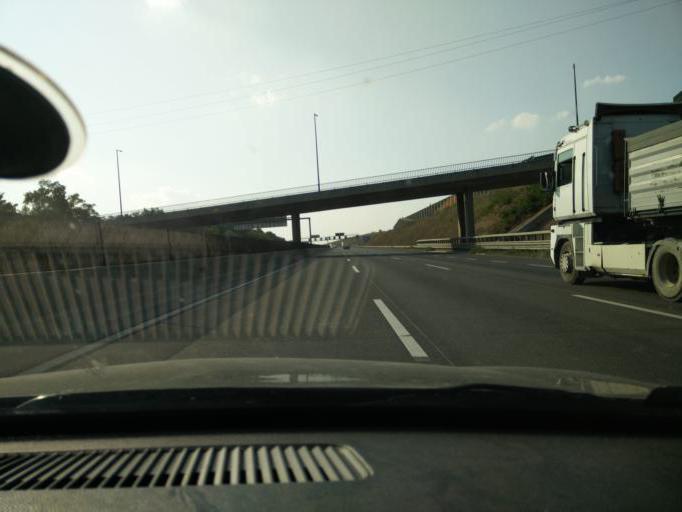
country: HU
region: Pest
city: Diosd
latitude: 47.4156
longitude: 18.9550
